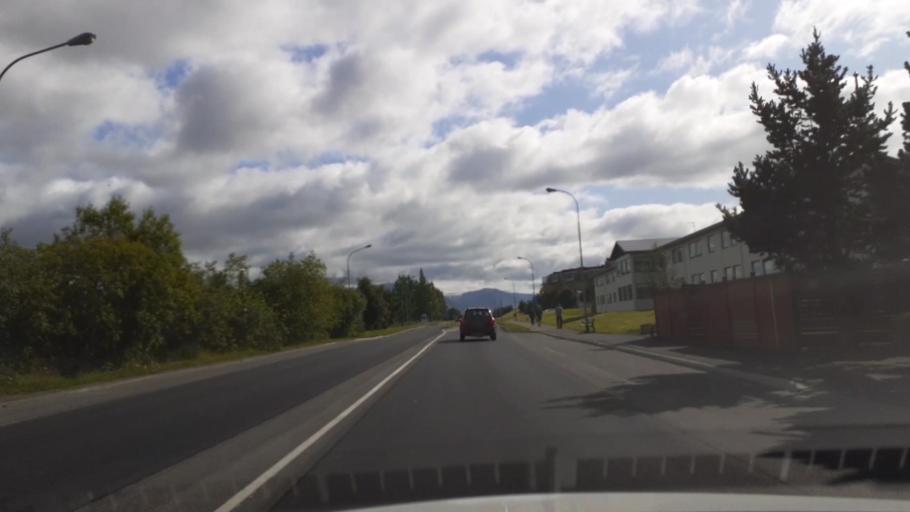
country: IS
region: Northeast
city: Akureyri
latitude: 65.6755
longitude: -18.0978
